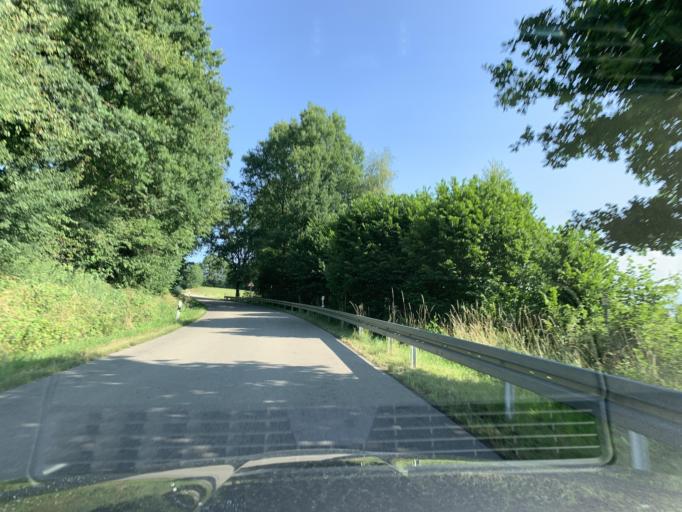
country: DE
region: Bavaria
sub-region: Upper Palatinate
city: Dieterskirchen
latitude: 49.4064
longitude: 12.4163
